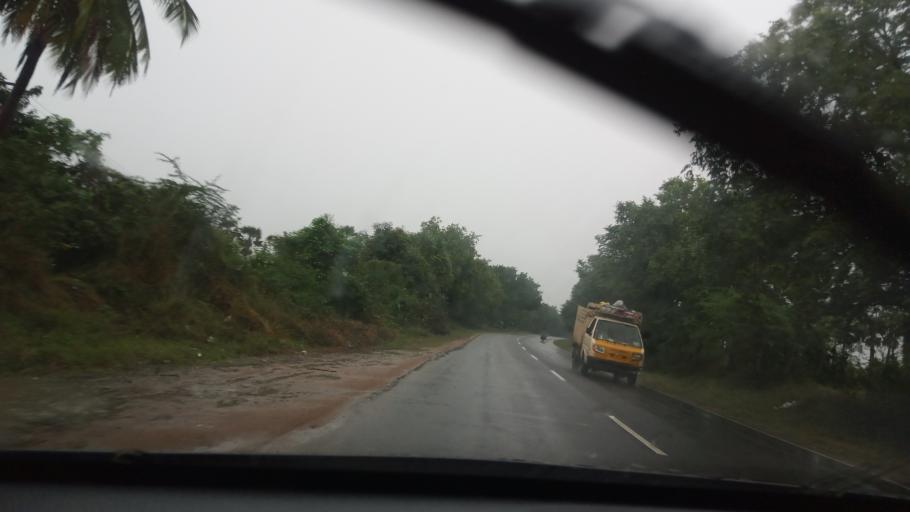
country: IN
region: Tamil Nadu
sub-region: Vellore
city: Kalavai
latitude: 12.8307
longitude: 79.4058
